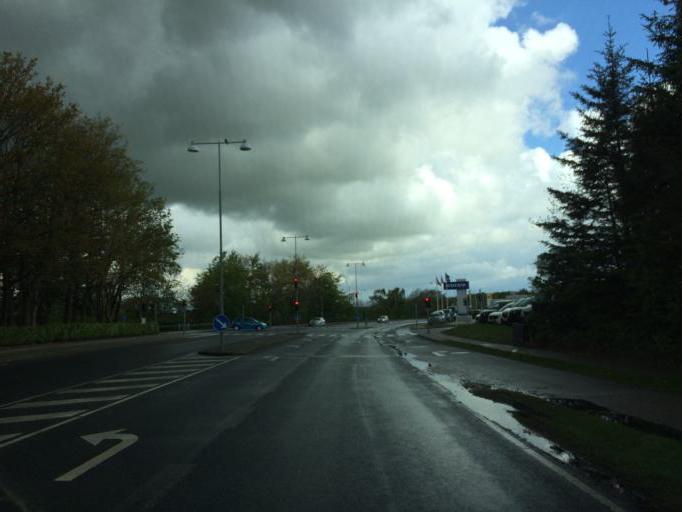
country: DK
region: Central Jutland
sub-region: Holstebro Kommune
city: Holstebro
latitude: 56.3733
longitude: 8.6113
